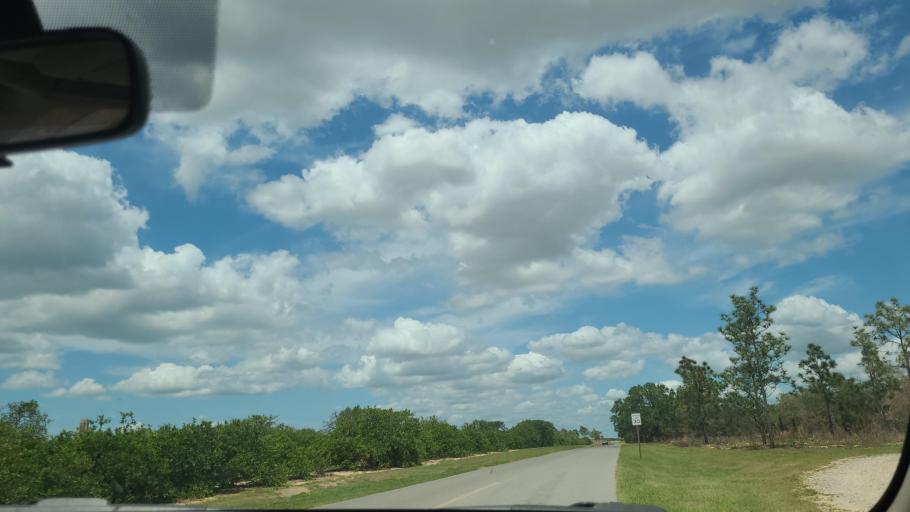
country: US
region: Florida
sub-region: Polk County
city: Lake Wales
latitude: 27.9269
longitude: -81.5695
